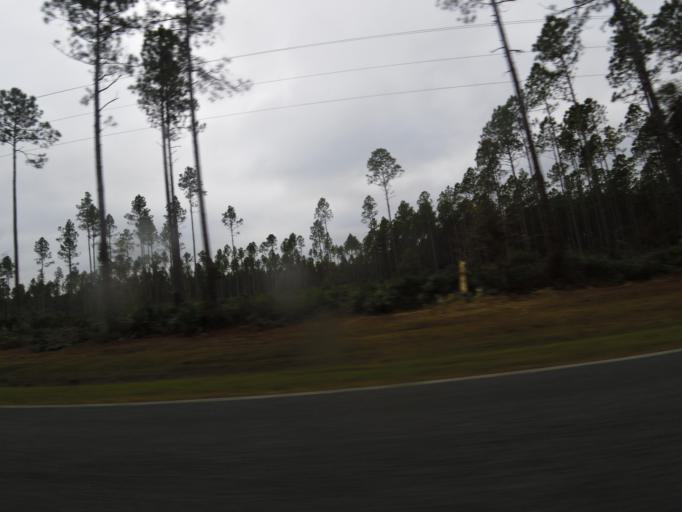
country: US
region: Georgia
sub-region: Charlton County
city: Folkston
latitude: 30.8864
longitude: -82.0588
